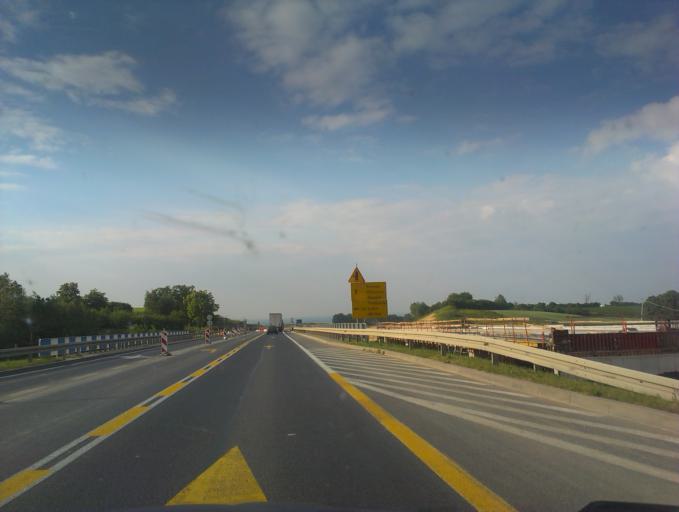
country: PL
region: Lower Silesian Voivodeship
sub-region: Powiat trzebnicki
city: Trzebnica
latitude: 51.3046
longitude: 17.0365
